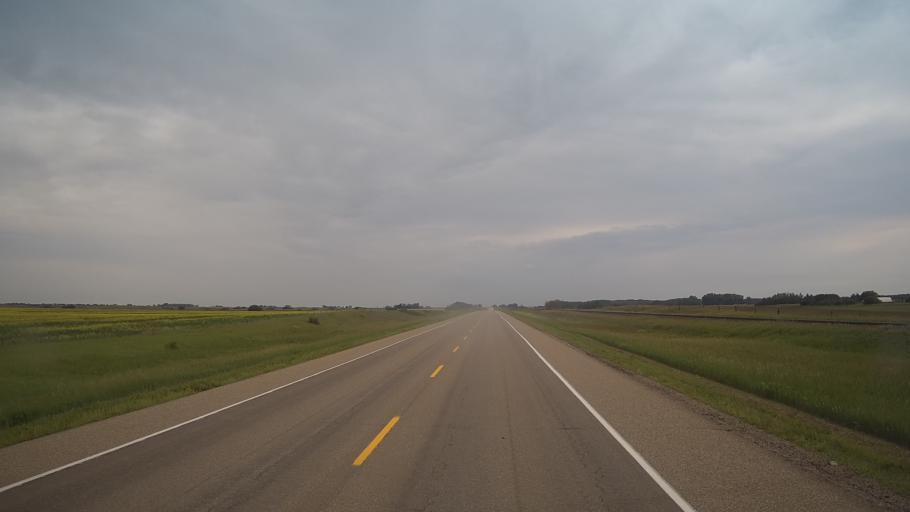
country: CA
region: Saskatchewan
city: Langham
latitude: 52.1275
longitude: -107.2546
